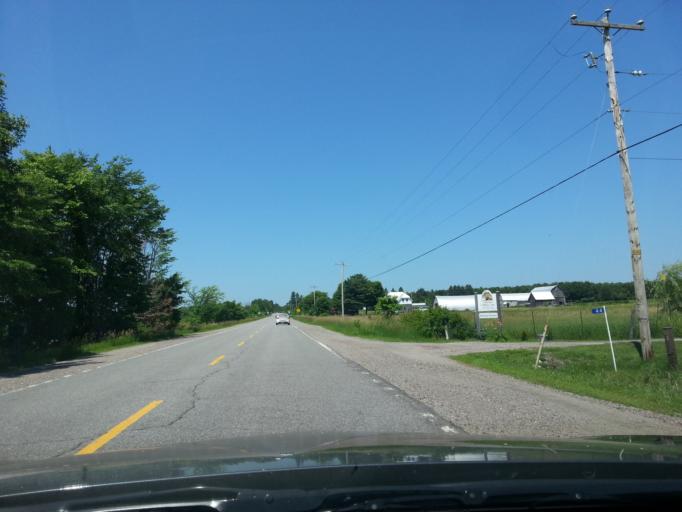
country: CA
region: Ontario
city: Arnprior
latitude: 45.5447
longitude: -76.3429
